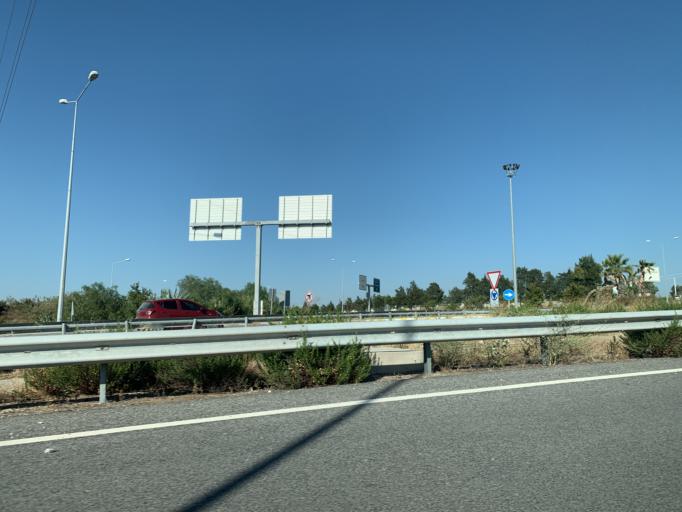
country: TR
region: Izmir
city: Urla
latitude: 38.3252
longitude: 26.7817
